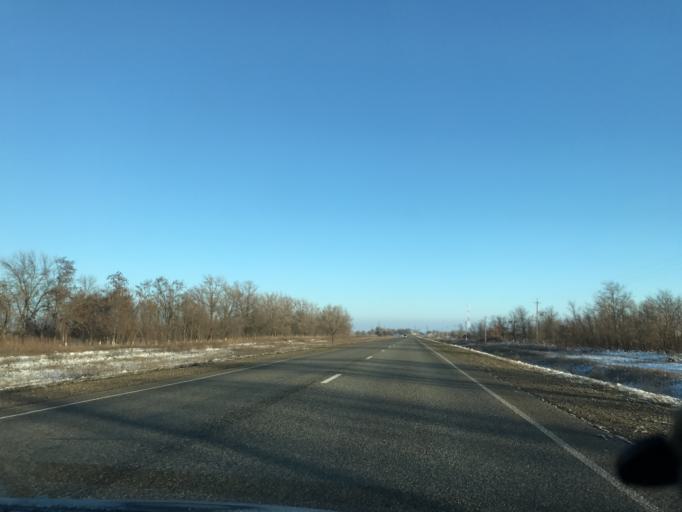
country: RU
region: Stavropol'skiy
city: Bezopasnoye
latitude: 45.6064
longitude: 41.9417
